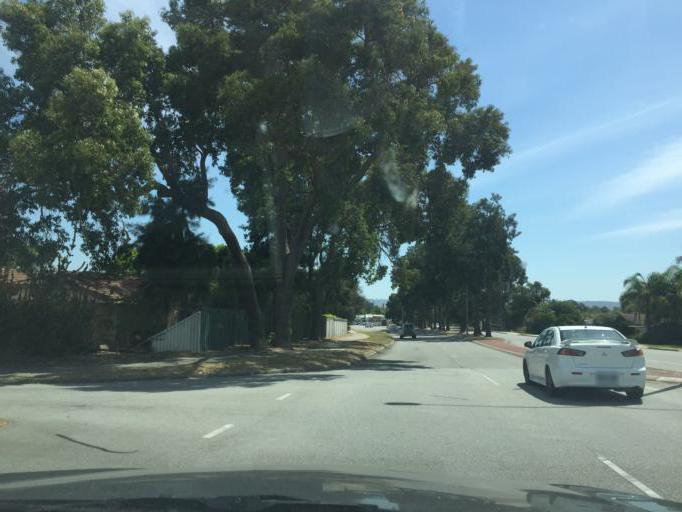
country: AU
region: Western Australia
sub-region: Gosnells
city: Thornlie
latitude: -32.0699
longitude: 115.9679
